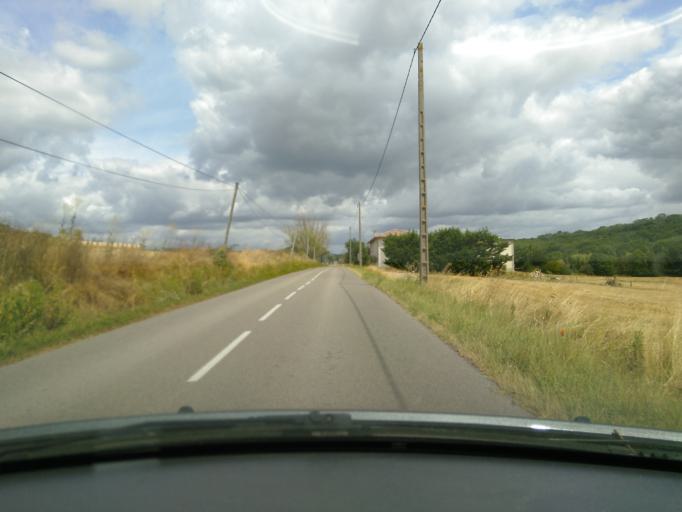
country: FR
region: Rhone-Alpes
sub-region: Departement de l'Isere
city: Beaurepaire
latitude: 45.3941
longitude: 5.0430
